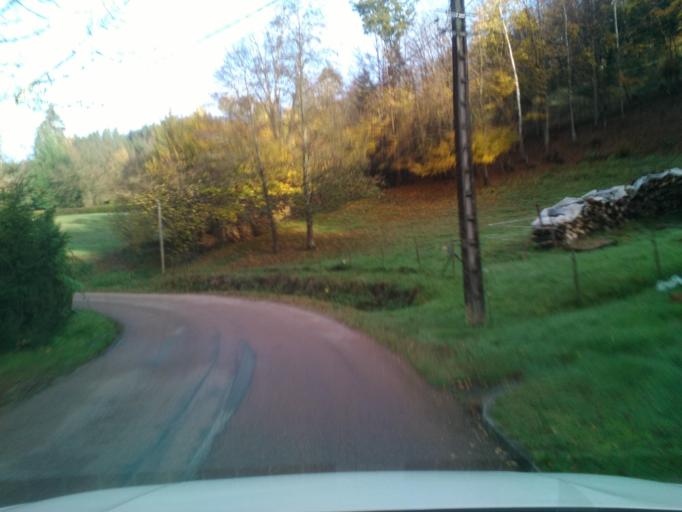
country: FR
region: Lorraine
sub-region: Departement des Vosges
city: Senones
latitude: 48.4230
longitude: 7.0383
